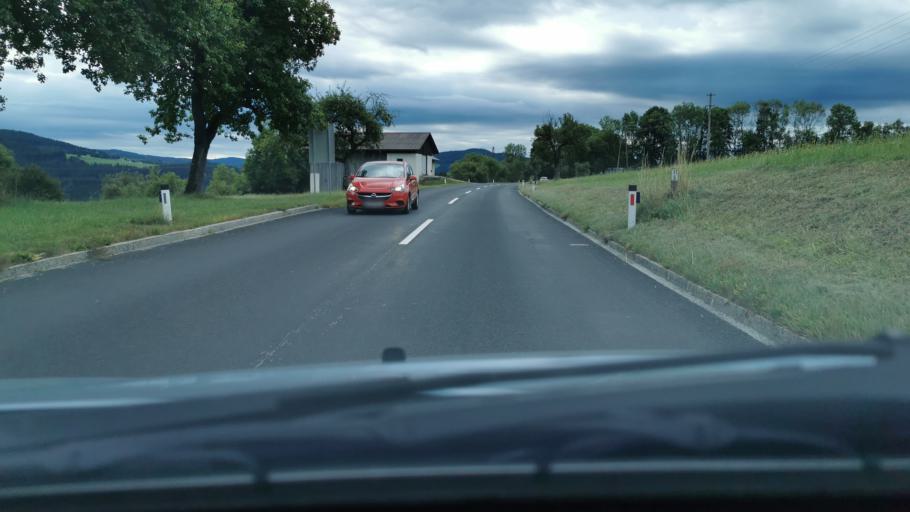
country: AT
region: Styria
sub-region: Politischer Bezirk Weiz
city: Birkfeld
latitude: 47.3863
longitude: 15.6742
